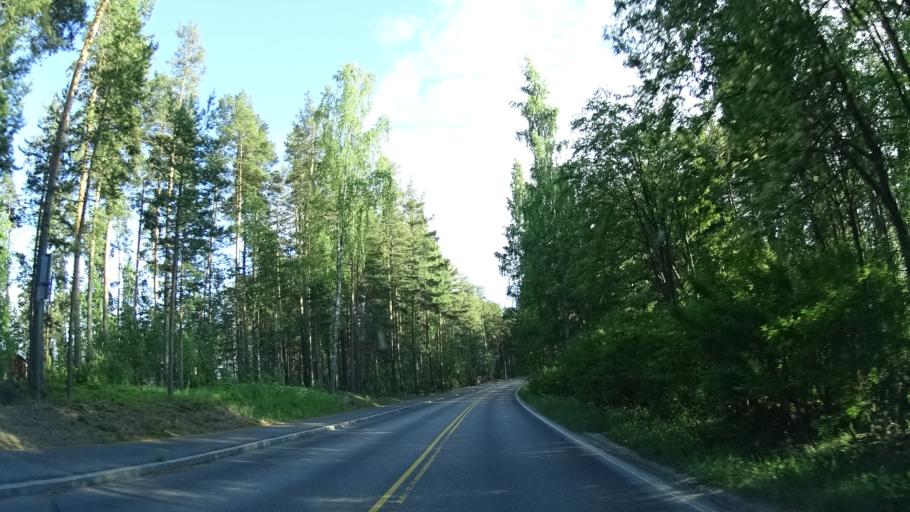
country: FI
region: Paijanne Tavastia
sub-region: Lahti
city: Asikkala
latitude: 61.3175
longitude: 25.5546
